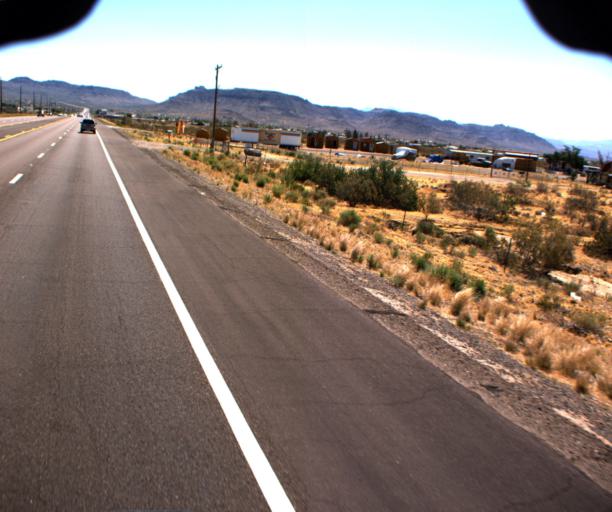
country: US
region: Arizona
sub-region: Mohave County
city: Golden Valley
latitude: 35.2206
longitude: -114.1891
